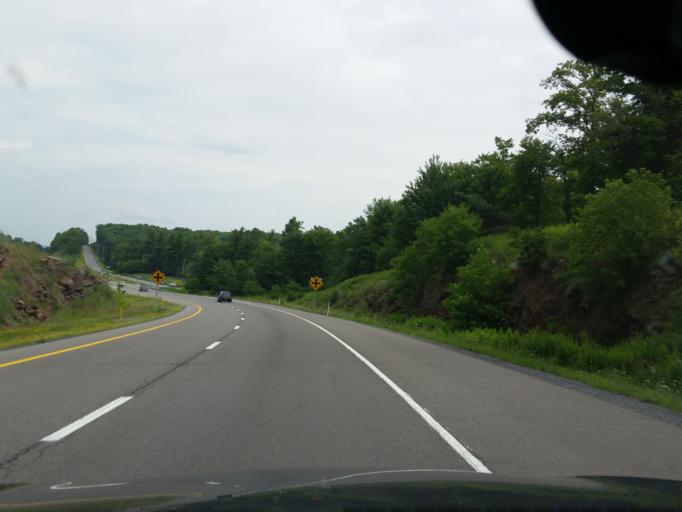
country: US
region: Pennsylvania
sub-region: Mifflin County
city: Milroy
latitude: 40.7604
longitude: -77.6142
